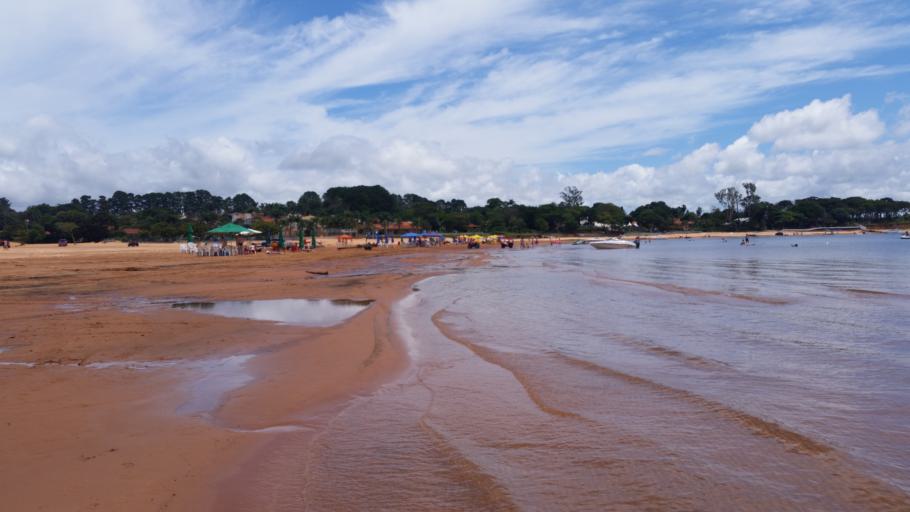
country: BR
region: Sao Paulo
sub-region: Itai
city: Itai
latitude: -23.2816
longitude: -49.0195
